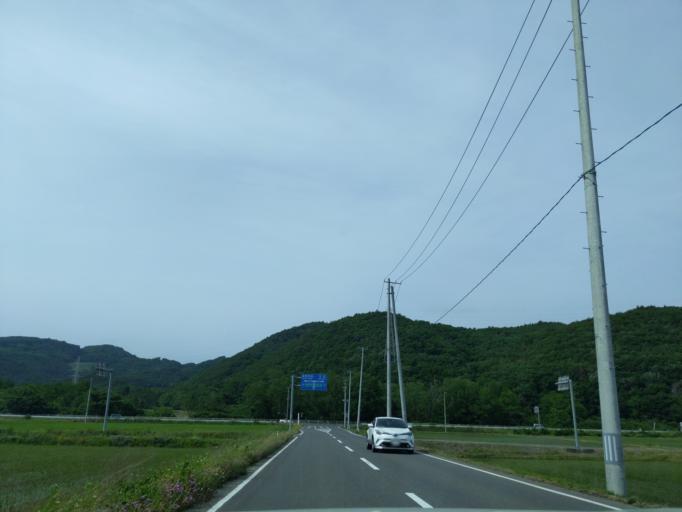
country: JP
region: Fukushima
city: Motomiya
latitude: 37.4757
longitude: 140.3168
